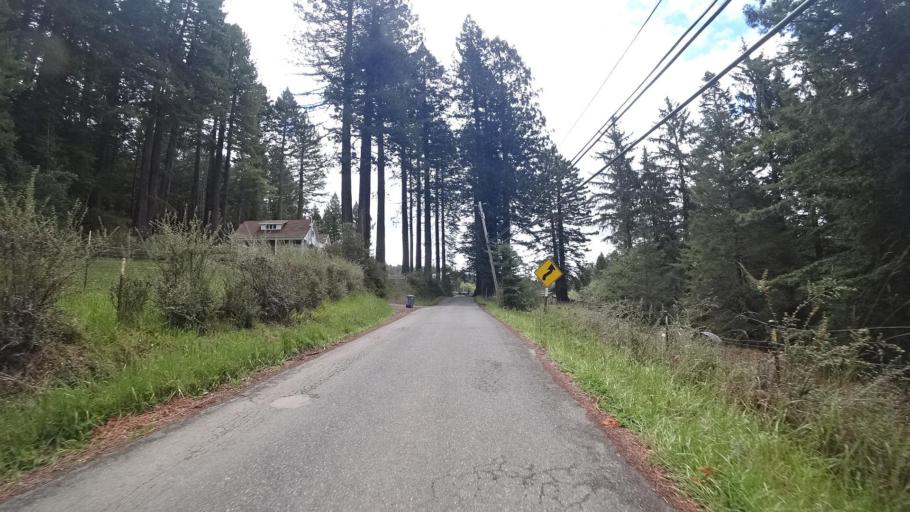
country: US
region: California
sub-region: Humboldt County
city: Bayside
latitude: 40.8395
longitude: -124.0238
